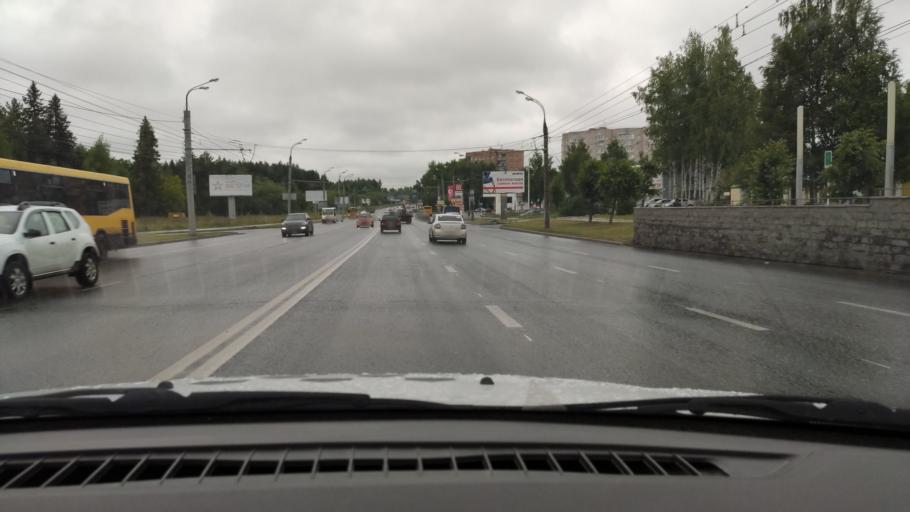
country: RU
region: Udmurtiya
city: Izhevsk
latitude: 56.8808
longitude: 53.2244
